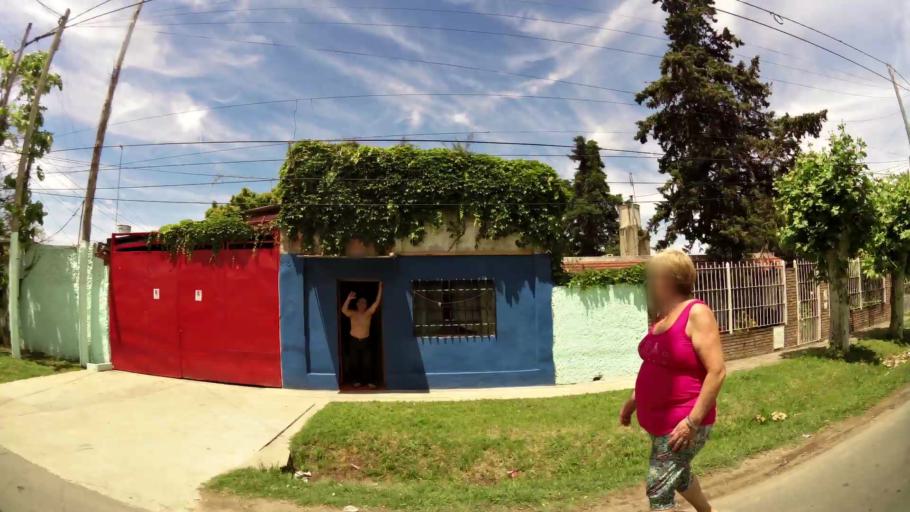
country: AR
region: Santa Fe
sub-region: Departamento de Rosario
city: Rosario
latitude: -32.9879
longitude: -60.6246
